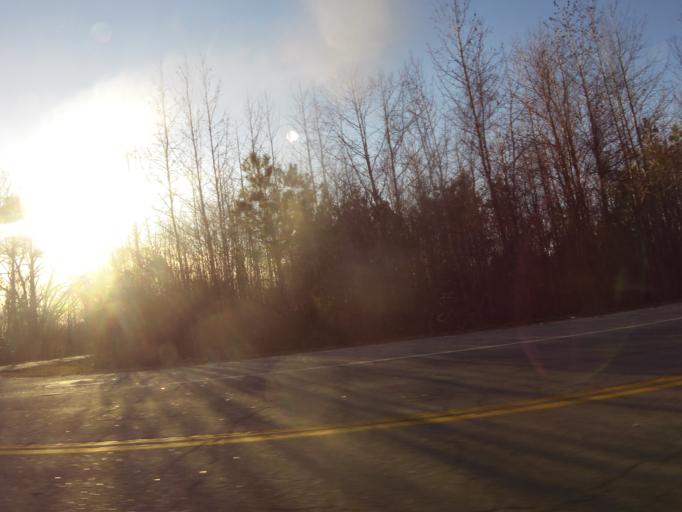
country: US
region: Virginia
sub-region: City of Franklin
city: Franklin
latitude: 36.6526
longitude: -76.8762
